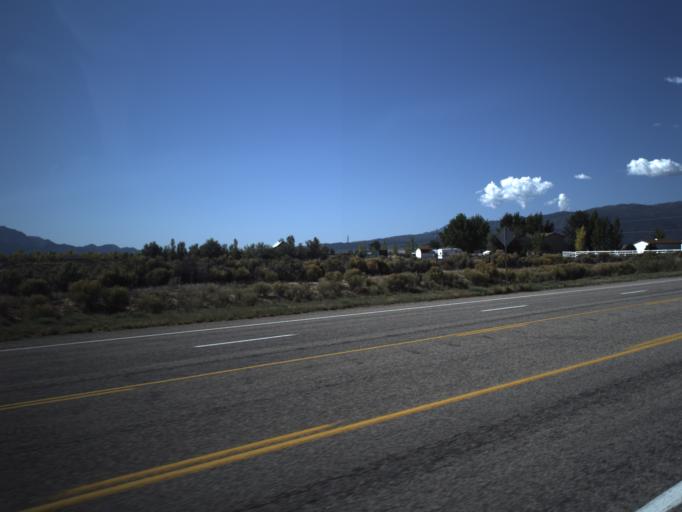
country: US
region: Utah
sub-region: Iron County
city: Cedar City
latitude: 37.6841
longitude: -113.1638
